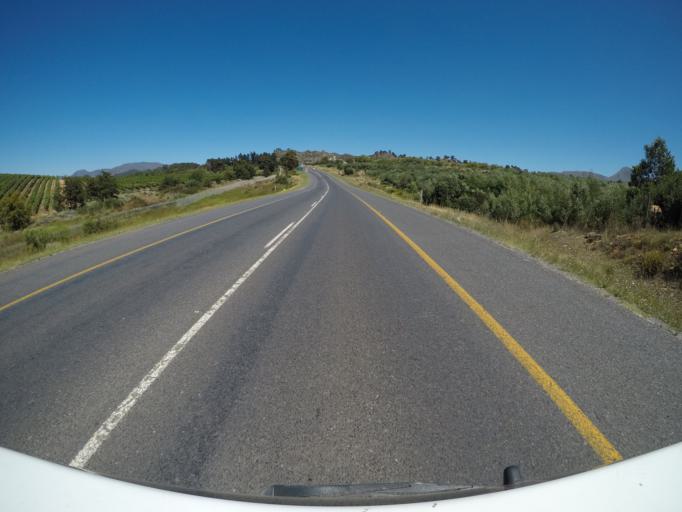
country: ZA
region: Western Cape
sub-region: Overberg District Municipality
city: Grabouw
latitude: -34.1624
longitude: 19.0146
